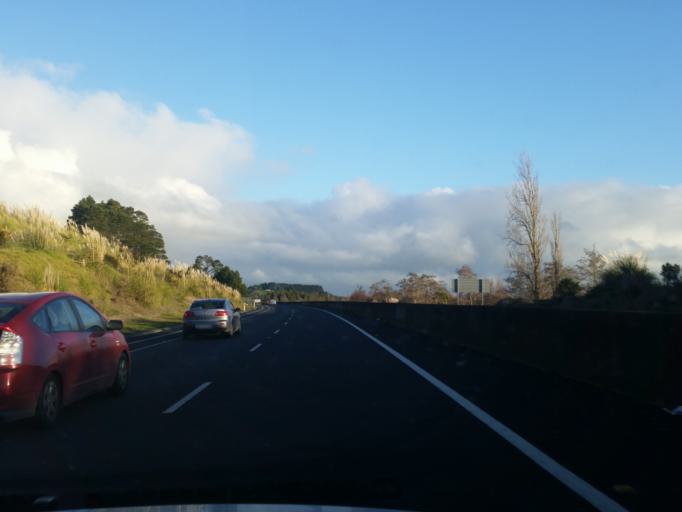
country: NZ
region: Waikato
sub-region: Waikato District
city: Te Kauwhata
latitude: -37.3144
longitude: 175.0666
